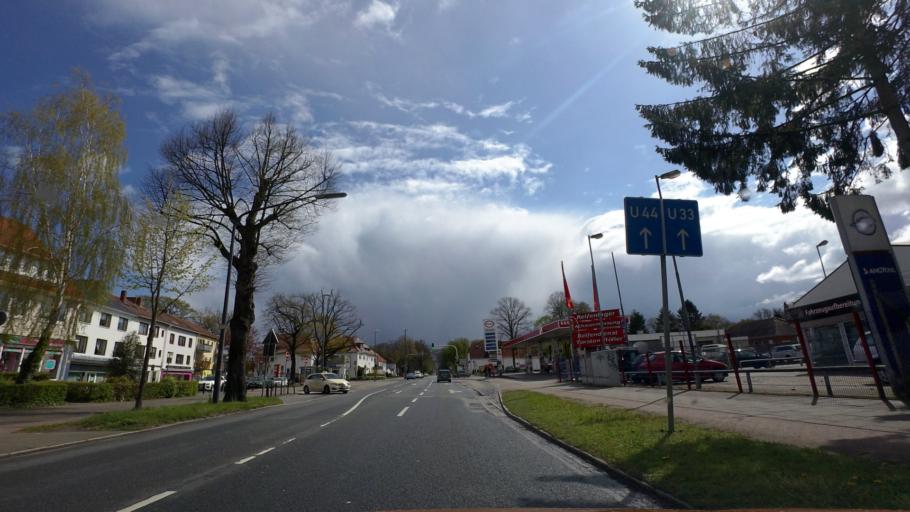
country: DE
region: Lower Saxony
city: Lilienthal
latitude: 53.0591
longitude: 8.9291
